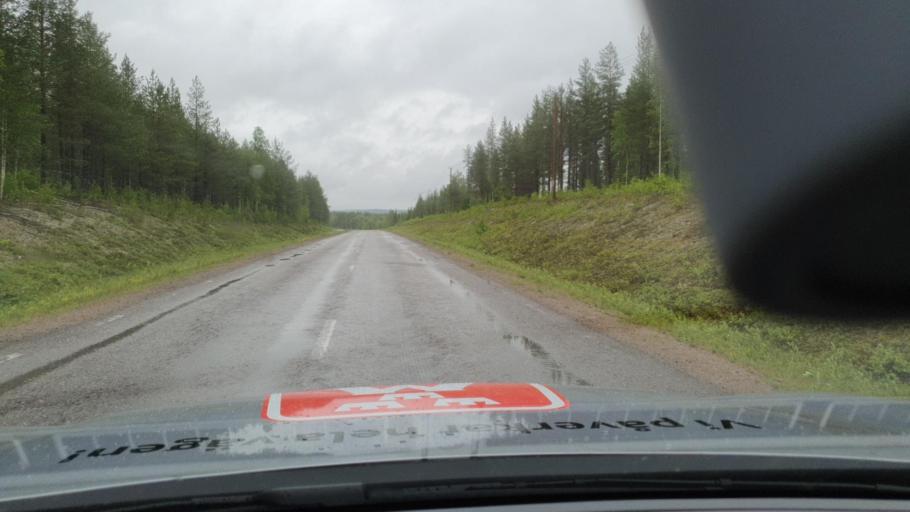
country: SE
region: Norrbotten
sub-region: Overkalix Kommun
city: OEverkalix
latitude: 66.4479
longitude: 23.1201
